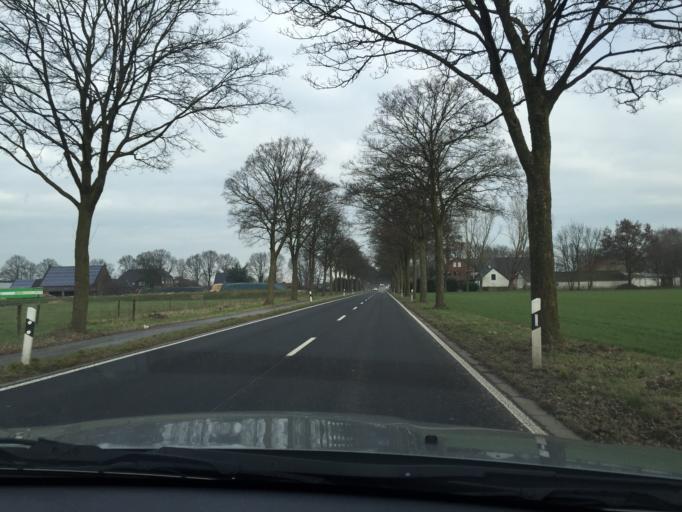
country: DE
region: North Rhine-Westphalia
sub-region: Regierungsbezirk Dusseldorf
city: Kleve
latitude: 51.7535
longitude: 6.1278
